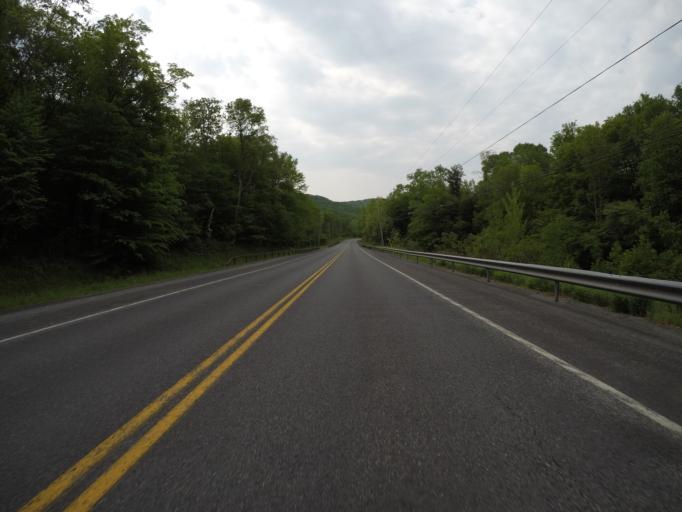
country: US
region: New York
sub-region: Sullivan County
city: Livingston Manor
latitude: 42.0195
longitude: -74.8919
